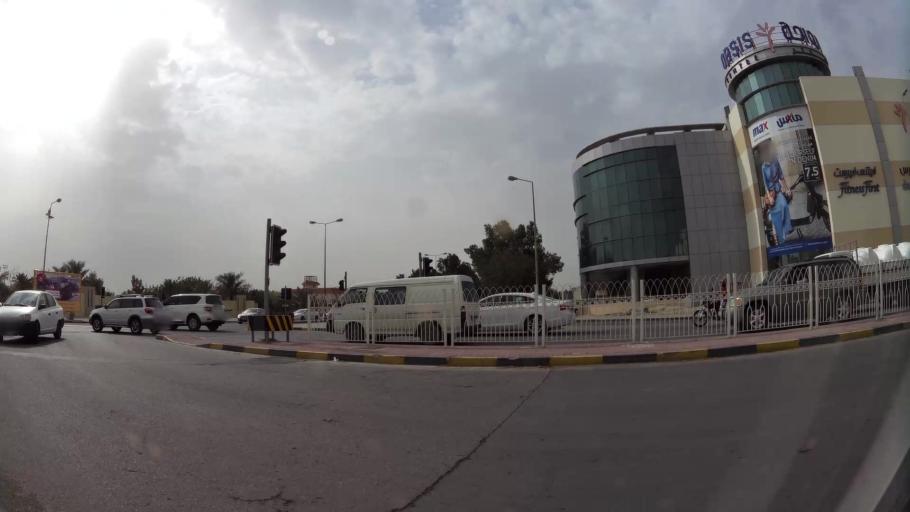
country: BH
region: Northern
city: Ar Rifa'
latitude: 26.1359
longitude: 50.5700
